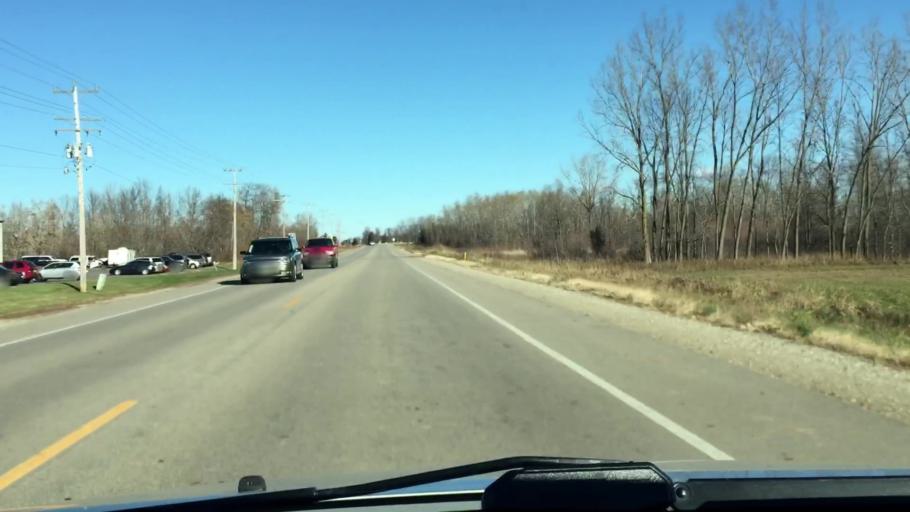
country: US
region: Wisconsin
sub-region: Brown County
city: Pulaski
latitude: 44.6827
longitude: -88.2427
